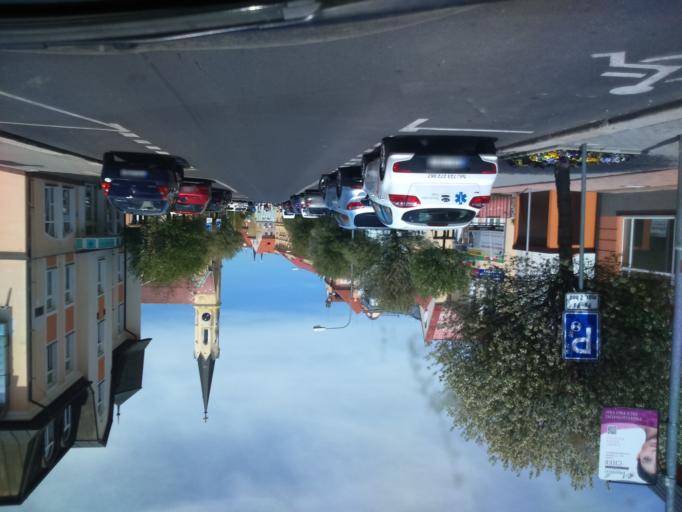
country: CZ
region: Karlovarsky
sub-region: Okres Cheb
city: Cheb
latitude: 50.0757
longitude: 12.3695
